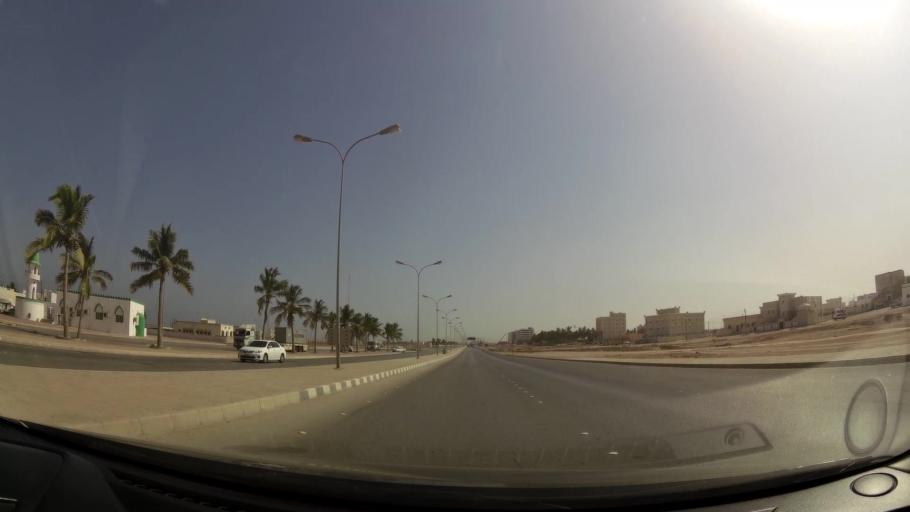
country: OM
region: Zufar
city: Salalah
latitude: 17.0002
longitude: 54.0356
